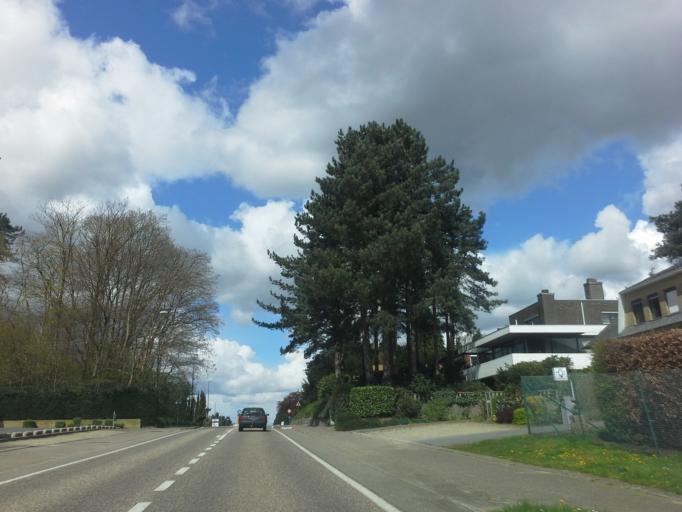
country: BE
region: Flanders
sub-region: Provincie Limburg
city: Tessenderlo
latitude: 51.0763
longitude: 5.0795
